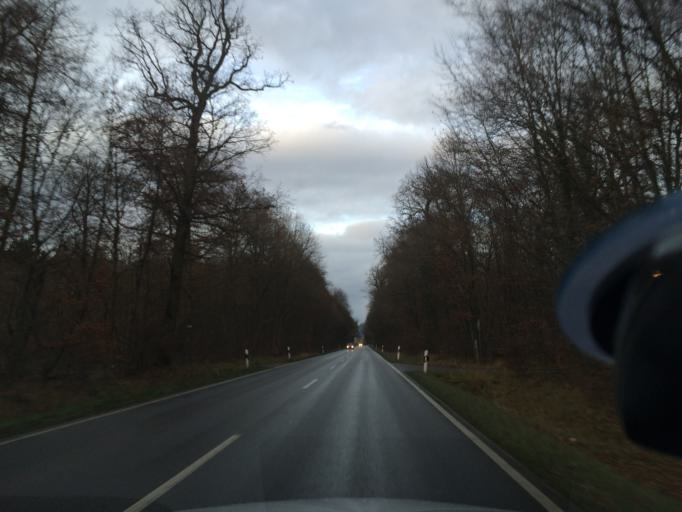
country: DE
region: Hesse
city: Morfelden-Walldorf
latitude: 49.9621
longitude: 8.5752
